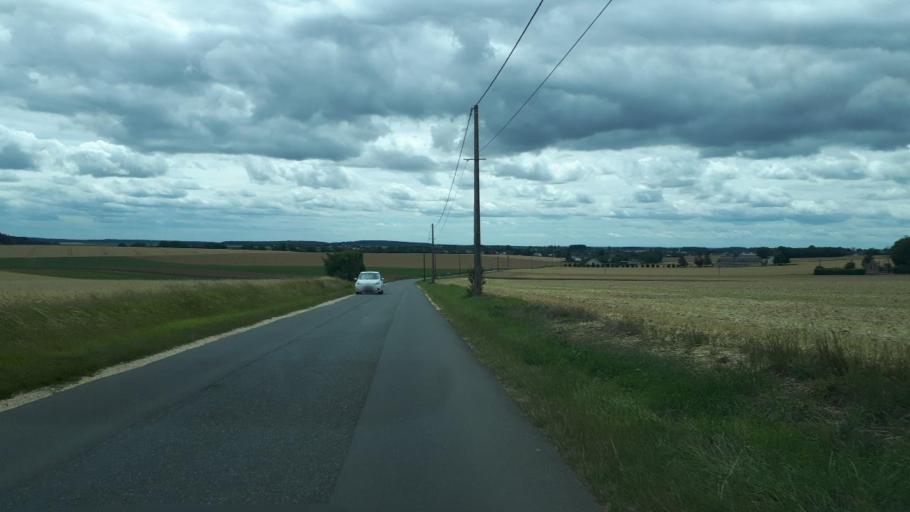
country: FR
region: Centre
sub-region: Departement du Cher
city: Rians
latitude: 47.2039
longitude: 2.6217
